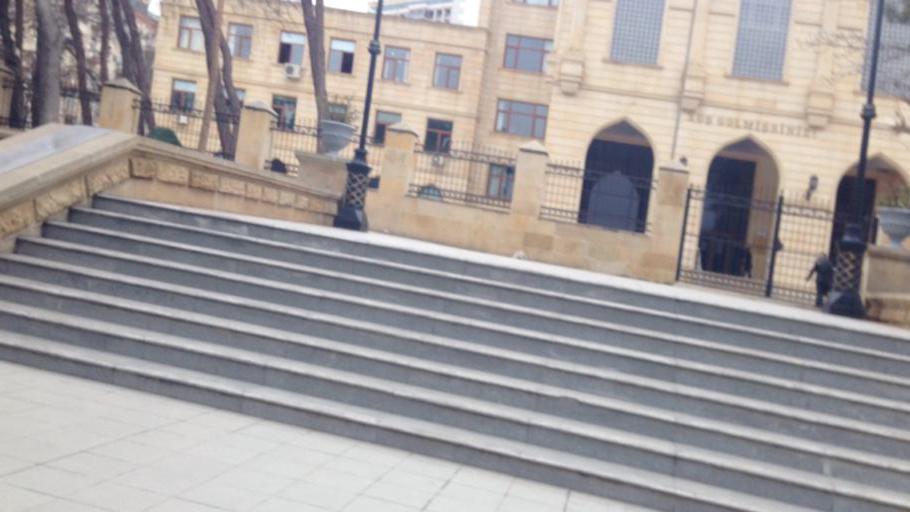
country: AZ
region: Baki
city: Badamdar
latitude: 40.3872
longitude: 49.8264
